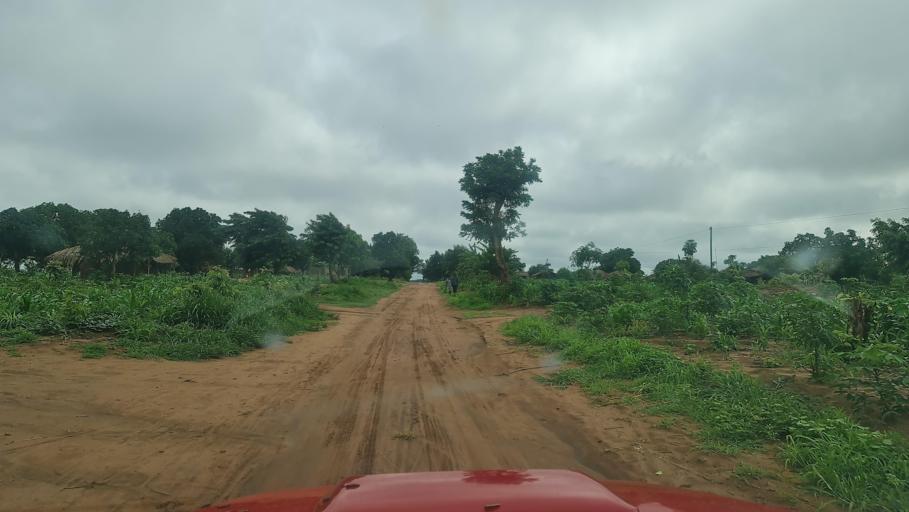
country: MW
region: Southern Region
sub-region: Nsanje District
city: Nsanje
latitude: -17.2047
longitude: 35.6834
